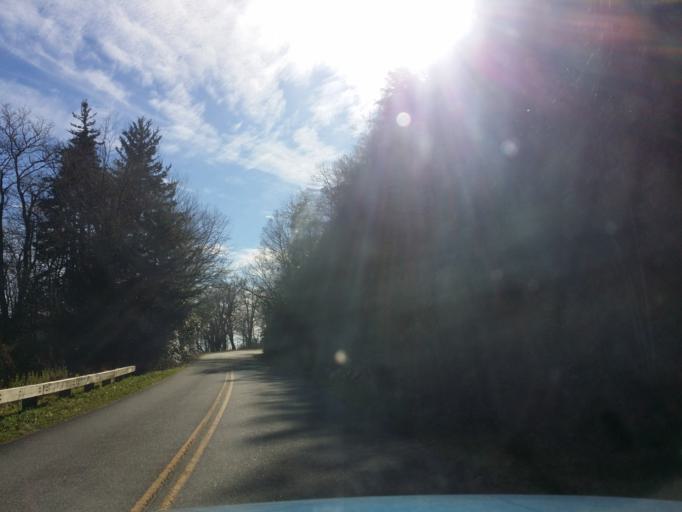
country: US
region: North Carolina
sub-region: Buncombe County
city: Black Mountain
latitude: 35.7217
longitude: -82.2206
